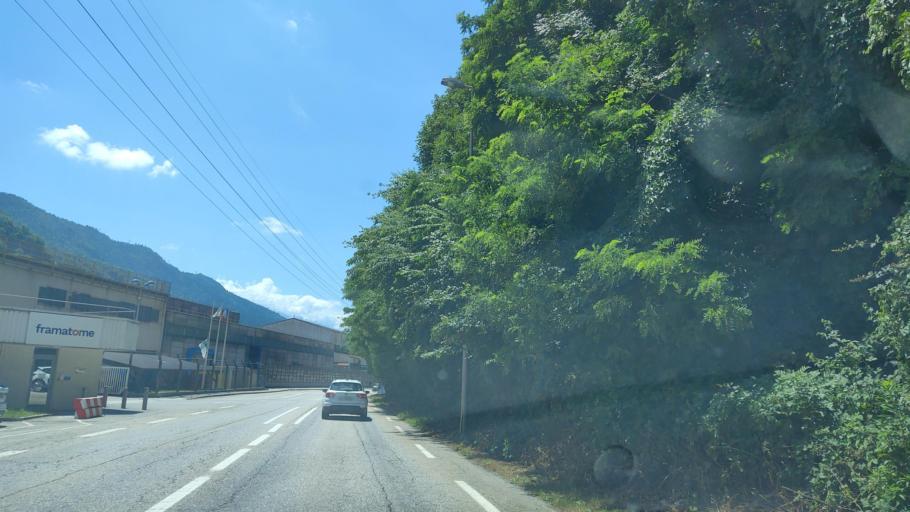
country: FR
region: Rhone-Alpes
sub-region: Departement de la Savoie
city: Ugine
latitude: 45.7497
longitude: 6.4318
